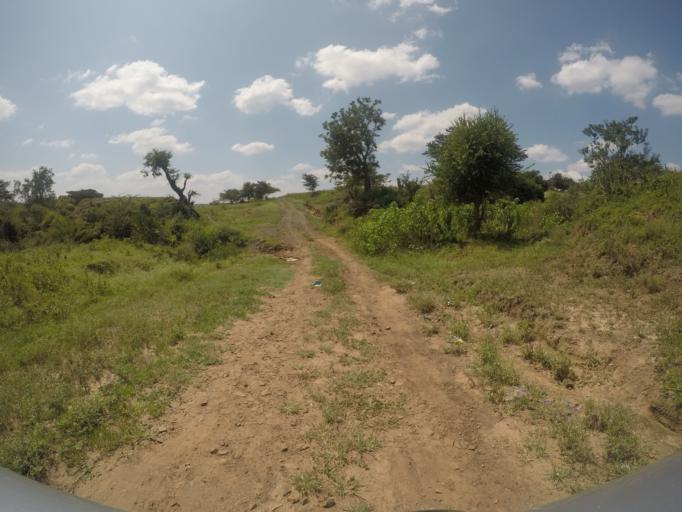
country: ZA
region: KwaZulu-Natal
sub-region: uThungulu District Municipality
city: Empangeni
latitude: -28.5947
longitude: 31.7357
